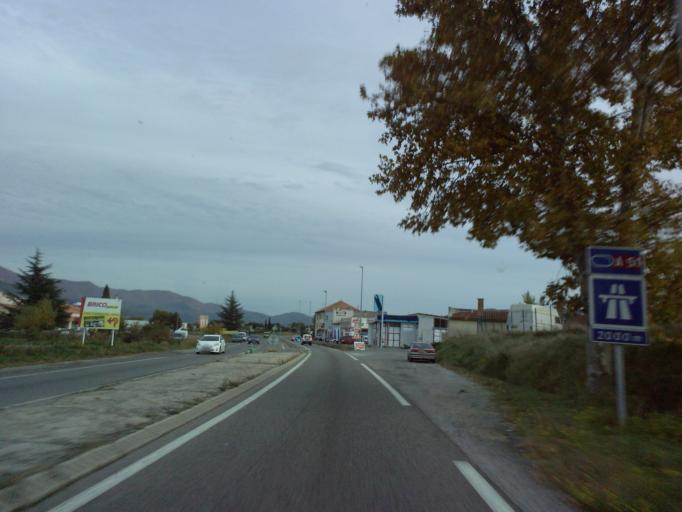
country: FR
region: Provence-Alpes-Cote d'Azur
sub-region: Departement des Alpes-de-Haute-Provence
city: Peipin
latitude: 44.1414
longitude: 5.9657
